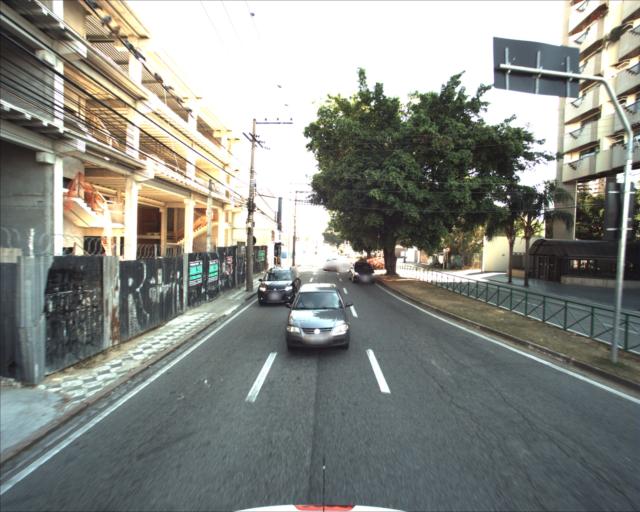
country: BR
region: Sao Paulo
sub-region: Sorocaba
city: Sorocaba
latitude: -23.5045
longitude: -47.4652
